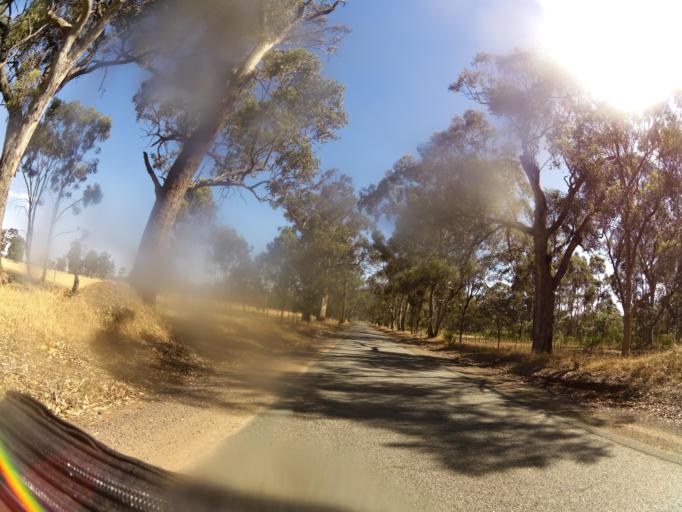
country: AU
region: Victoria
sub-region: Campaspe
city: Kyabram
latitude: -36.8744
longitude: 145.0858
